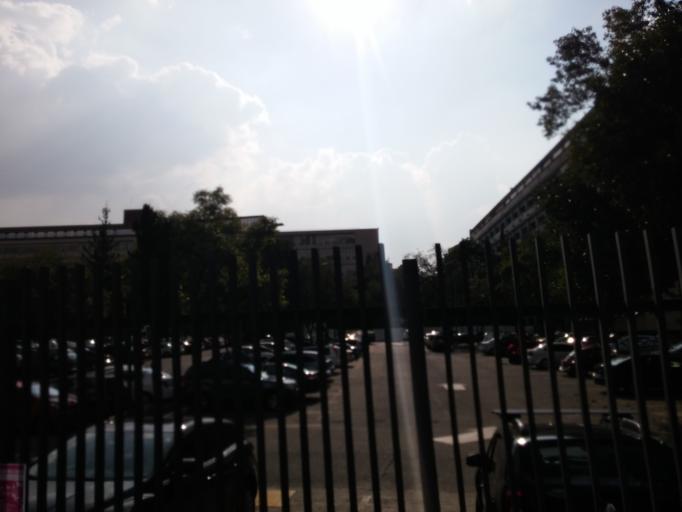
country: MX
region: Mexico City
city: Coyoacan
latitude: 19.3337
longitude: -99.1788
